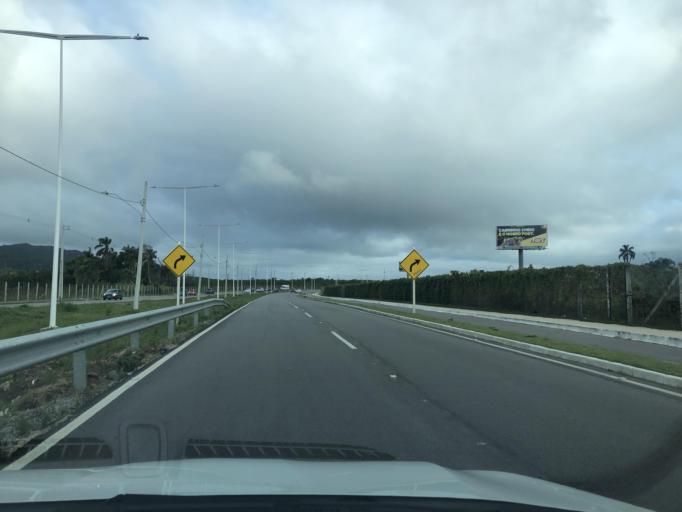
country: BR
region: Santa Catarina
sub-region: Florianopolis
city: Carianos
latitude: -27.6643
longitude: -48.5253
